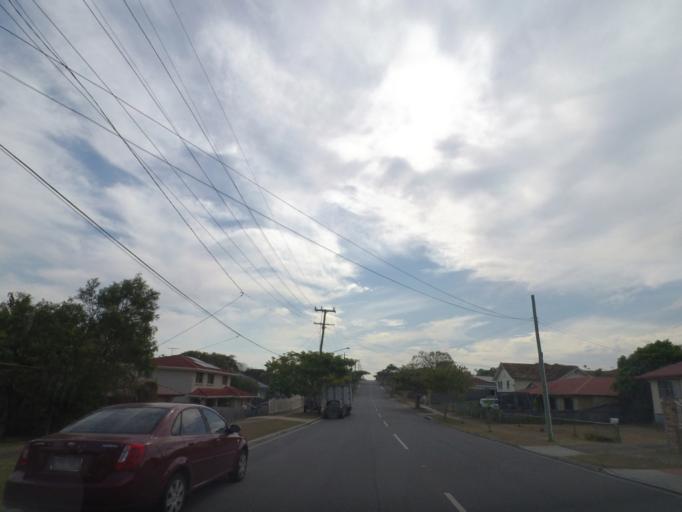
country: AU
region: Queensland
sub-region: Brisbane
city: Inala
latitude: -27.5891
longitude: 152.9755
